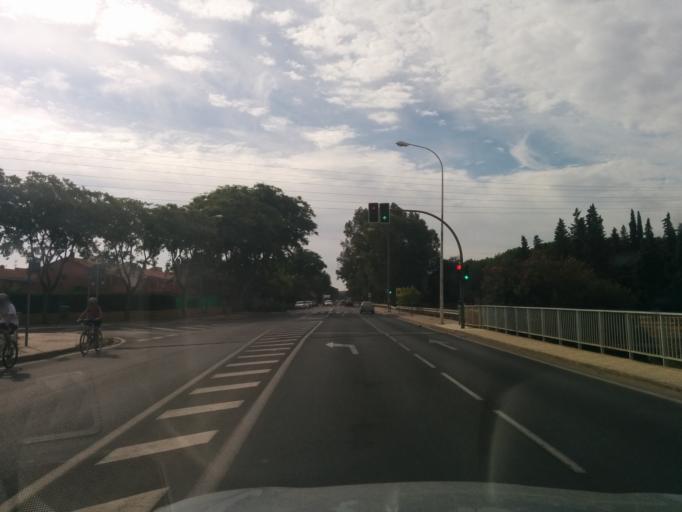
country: ES
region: Andalusia
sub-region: Provincia de Sevilla
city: Sevilla
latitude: 37.4013
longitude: -5.9330
